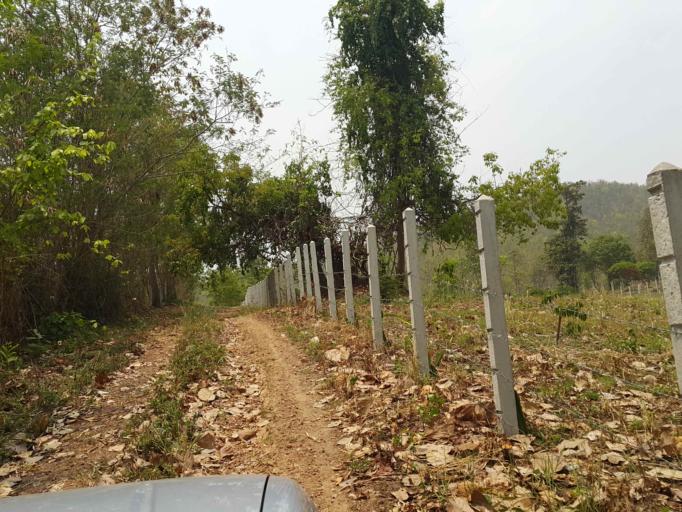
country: TH
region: Chiang Mai
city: San Sai
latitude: 18.9395
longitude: 99.0386
